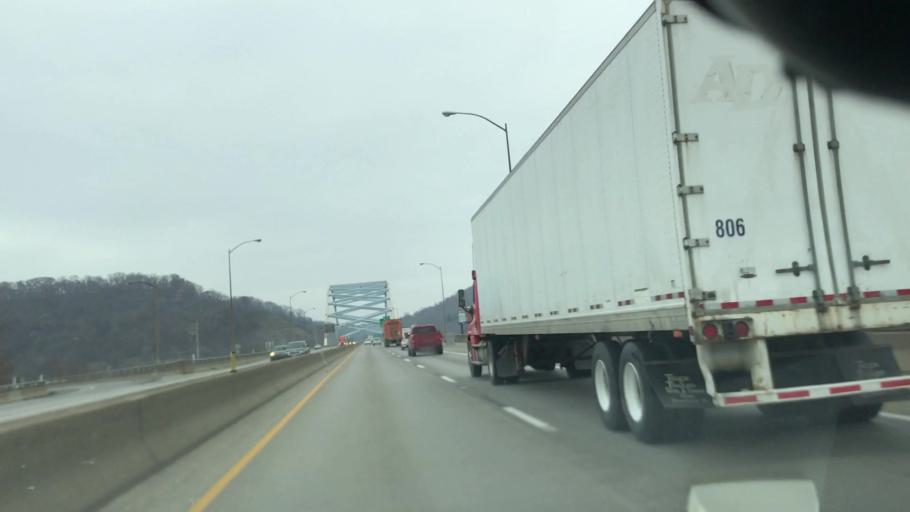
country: US
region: Pennsylvania
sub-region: Allegheny County
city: Coraopolis
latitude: 40.5109
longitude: -80.1356
